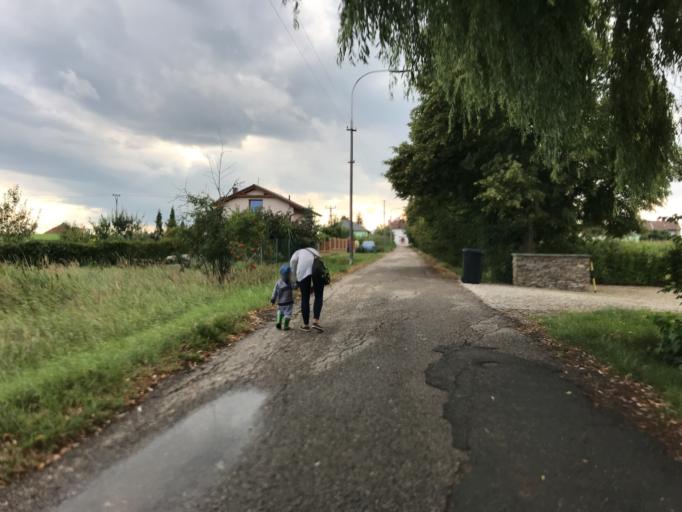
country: CZ
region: Jihocesky
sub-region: Okres Jindrichuv Hradec
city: Trebon
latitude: 49.0123
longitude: 14.7524
